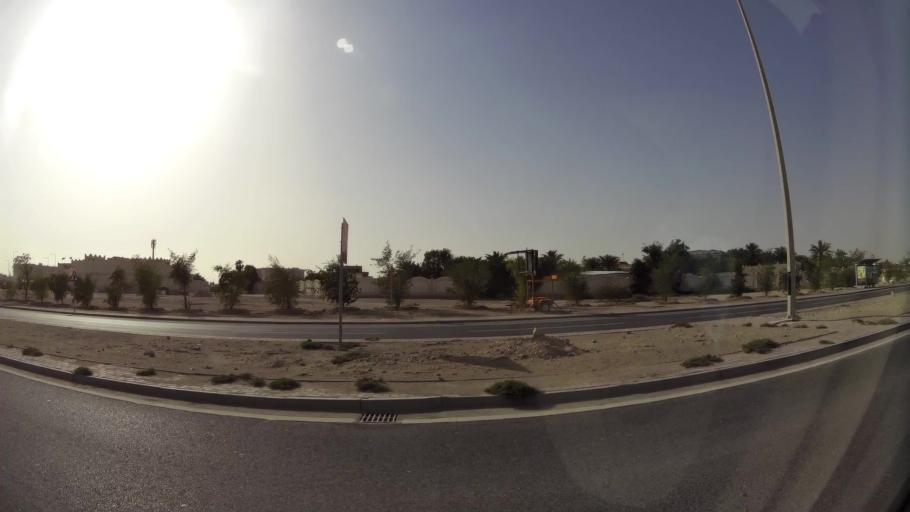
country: QA
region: Baladiyat ar Rayyan
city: Ar Rayyan
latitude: 25.3260
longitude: 51.4242
